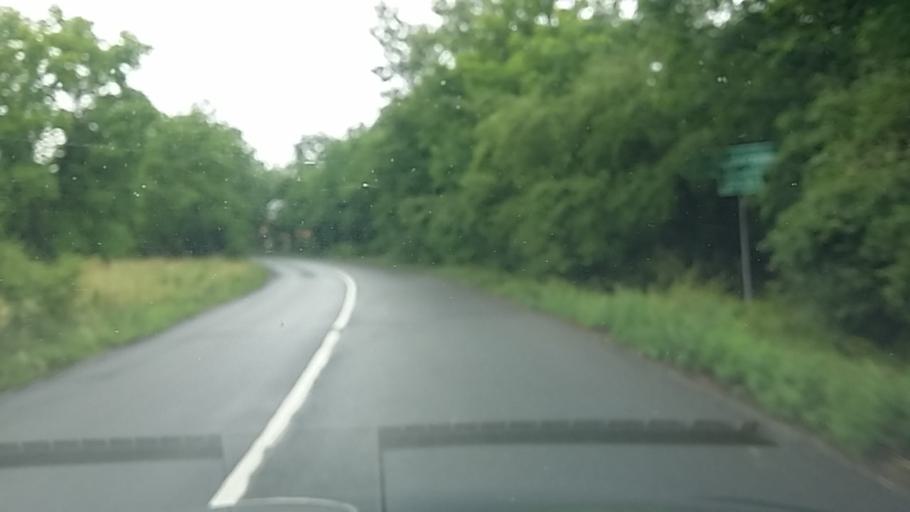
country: HU
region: Pest
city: Szob
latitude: 47.9448
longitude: 18.7786
